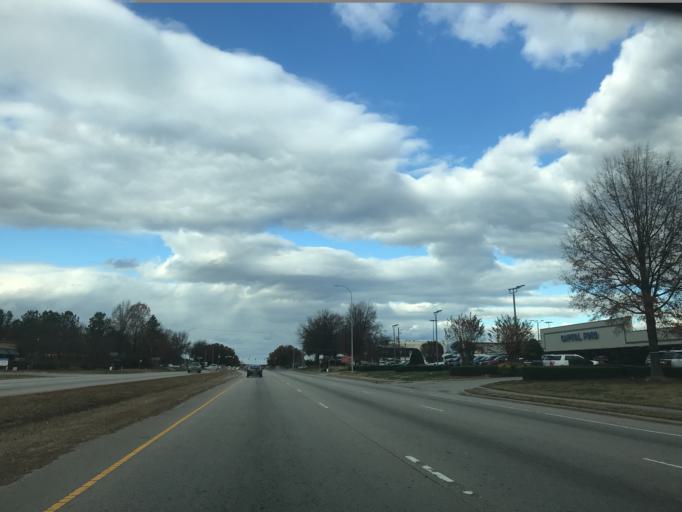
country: US
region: North Carolina
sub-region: Wake County
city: Raleigh
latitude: 35.8521
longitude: -78.5807
